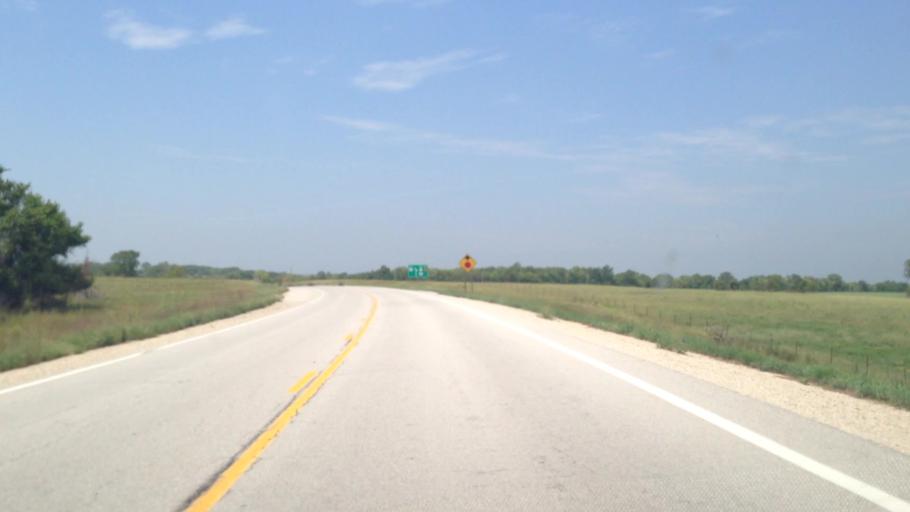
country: US
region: Kansas
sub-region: Anderson County
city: Garnett
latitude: 38.1951
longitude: -95.2450
